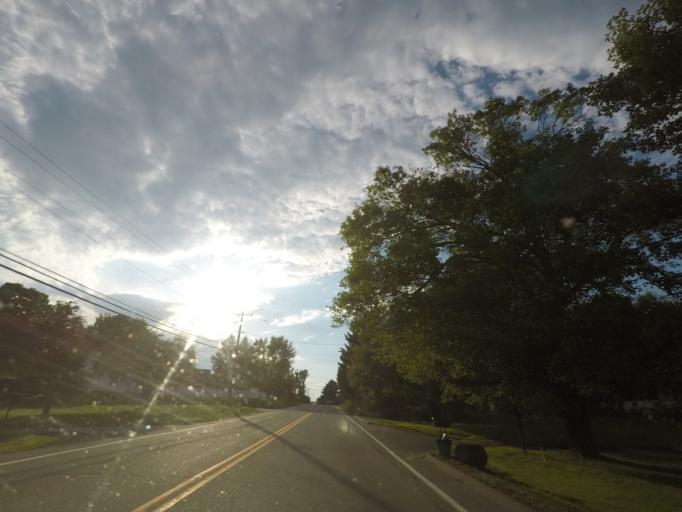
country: US
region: Connecticut
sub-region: Windham County
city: Quinebaug
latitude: 42.0209
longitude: -71.9436
